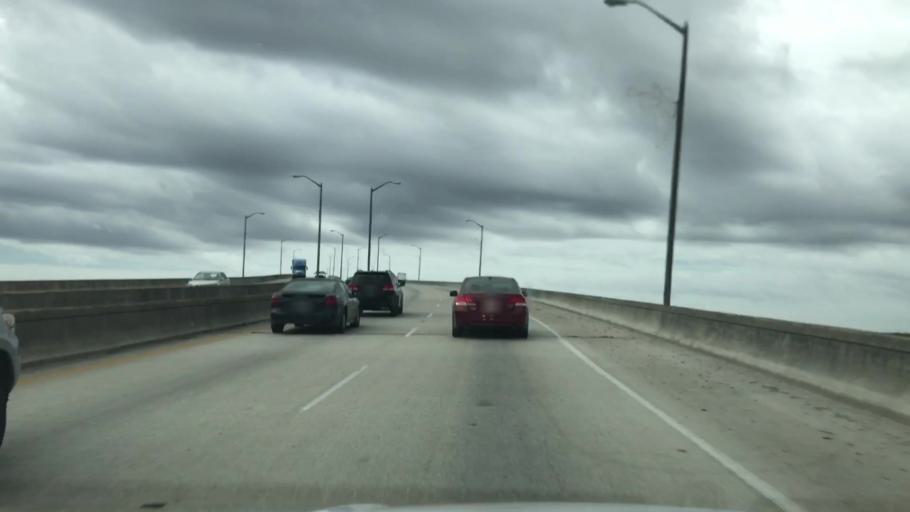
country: US
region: South Carolina
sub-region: Georgetown County
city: Georgetown
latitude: 33.3621
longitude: -79.2955
